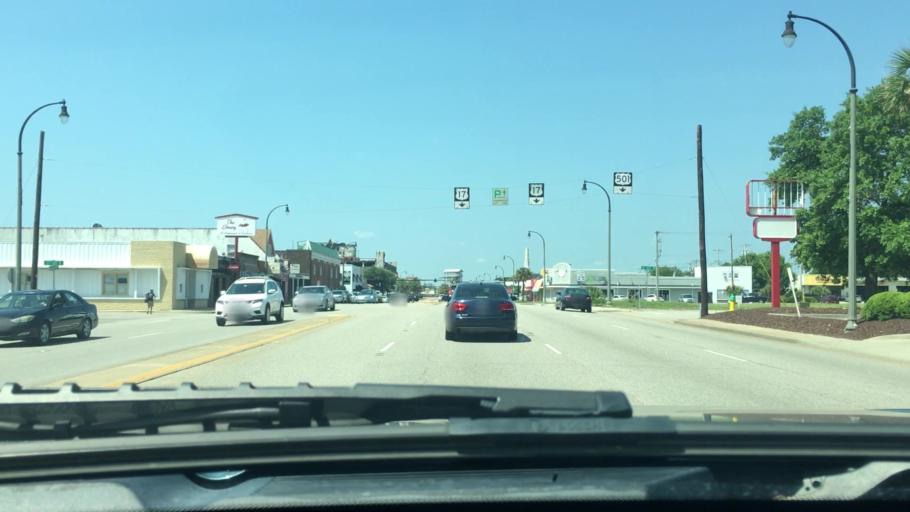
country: US
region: South Carolina
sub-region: Horry County
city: Myrtle Beach
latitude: 33.6971
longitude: -78.8783
